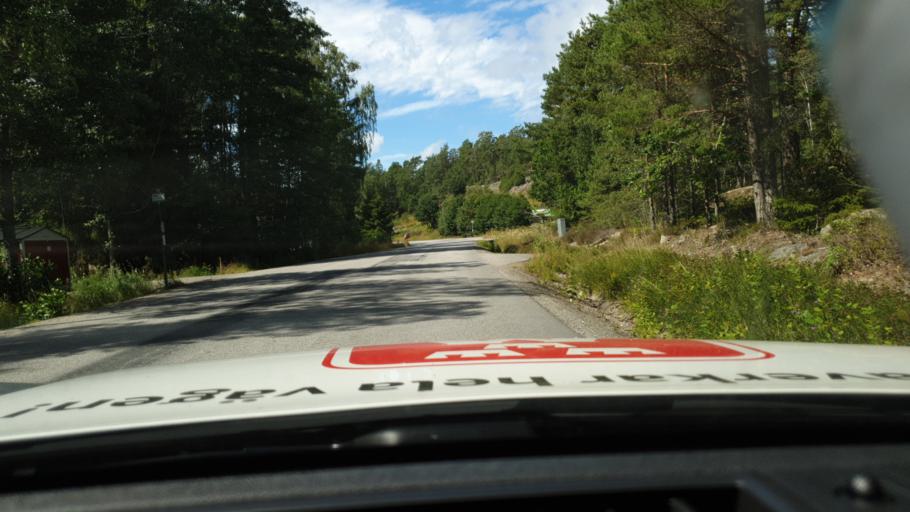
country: SE
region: Stockholm
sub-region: Haninge Kommun
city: Jordbro
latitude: 59.0248
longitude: 18.1631
